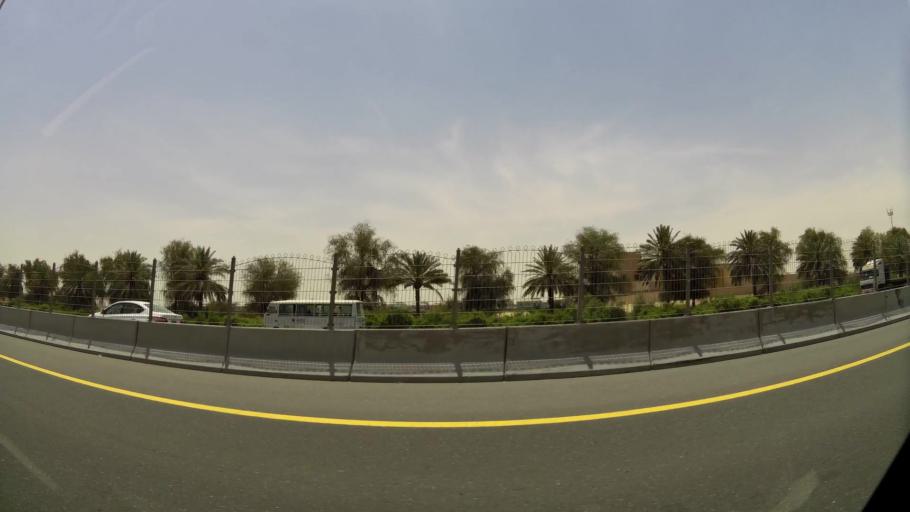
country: AE
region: Dubai
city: Dubai
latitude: 25.1048
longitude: 55.3386
